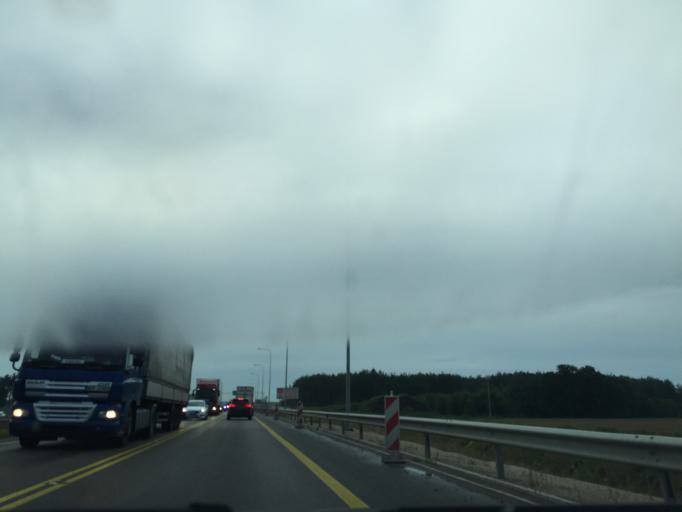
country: PL
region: Podlasie
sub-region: Powiat zambrowski
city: Szumowo
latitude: 52.9051
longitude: 22.0887
